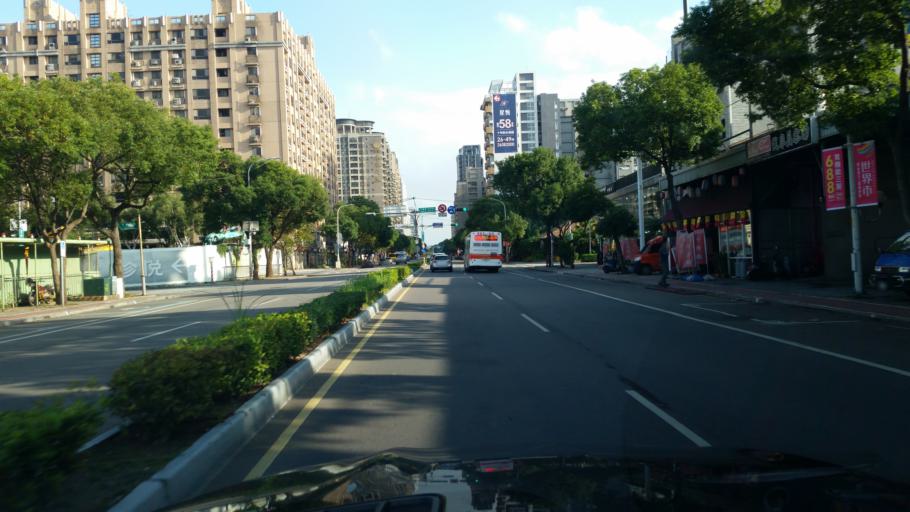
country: TW
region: Taiwan
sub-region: Taoyuan
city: Taoyuan
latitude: 25.0801
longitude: 121.3701
